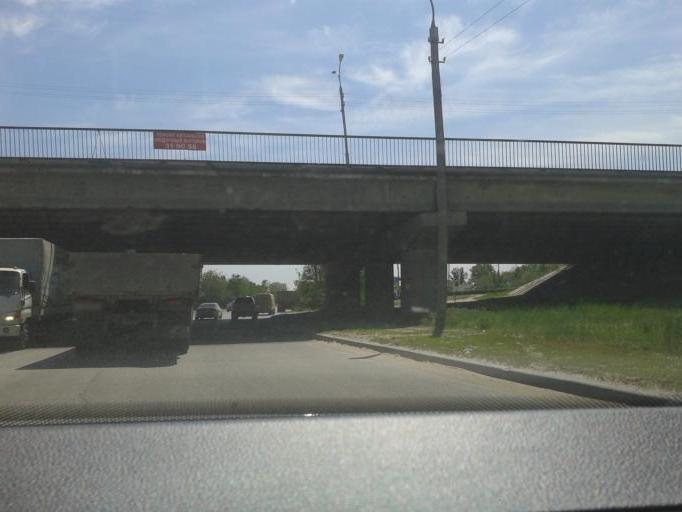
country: RU
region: Volgograd
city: Volgograd
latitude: 48.7656
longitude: 44.5151
